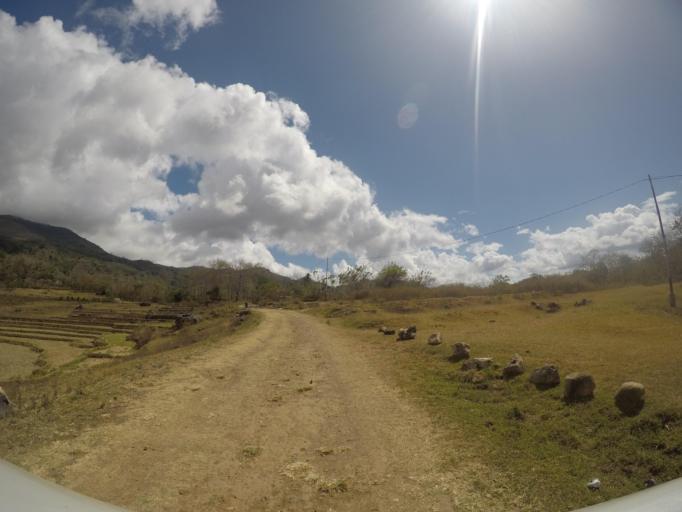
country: TL
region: Lautem
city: Lospalos
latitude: -8.5295
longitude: 126.8004
